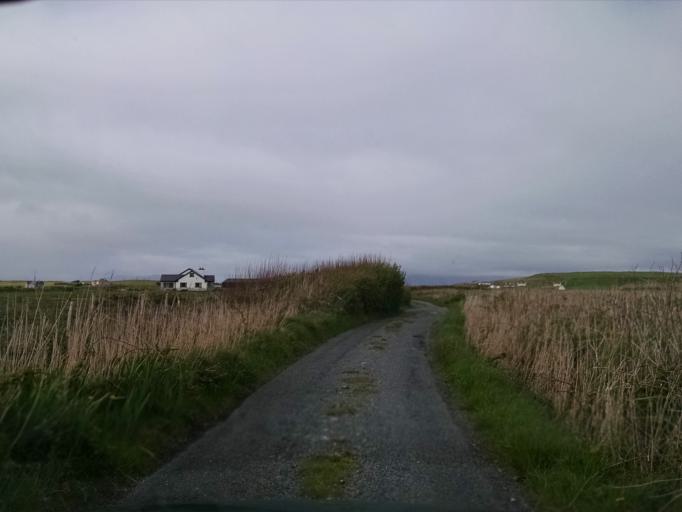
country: IE
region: Connaught
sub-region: County Galway
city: Clifden
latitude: 53.7512
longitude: -9.8799
